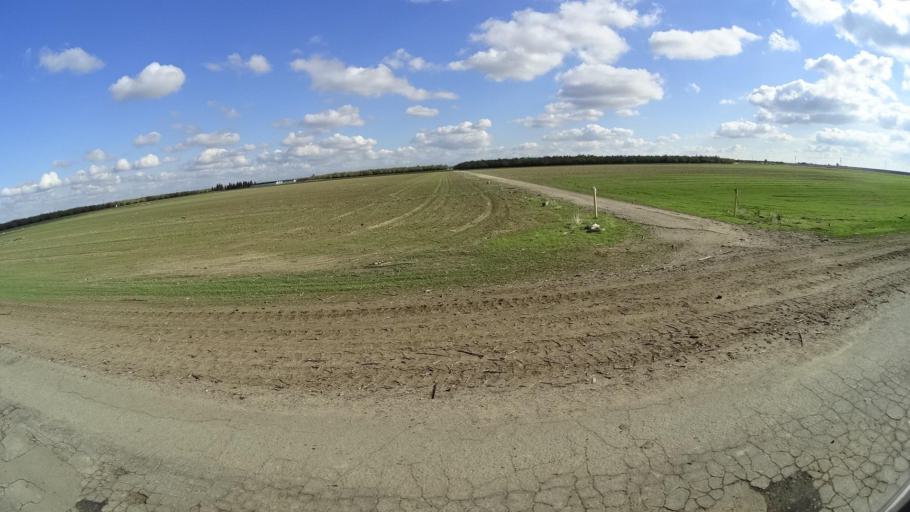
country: US
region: California
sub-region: Kern County
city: McFarland
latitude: 35.6788
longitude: -119.2686
